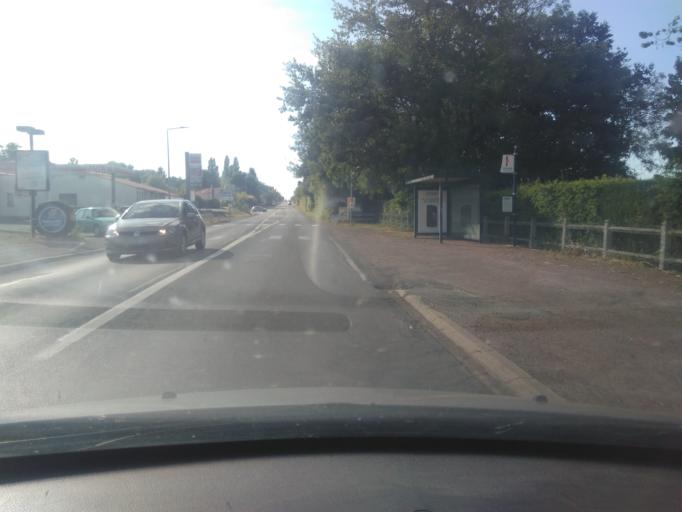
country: FR
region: Pays de la Loire
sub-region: Departement de la Vendee
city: Saint-Florent-des-Bois
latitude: 46.5956
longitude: -1.3191
